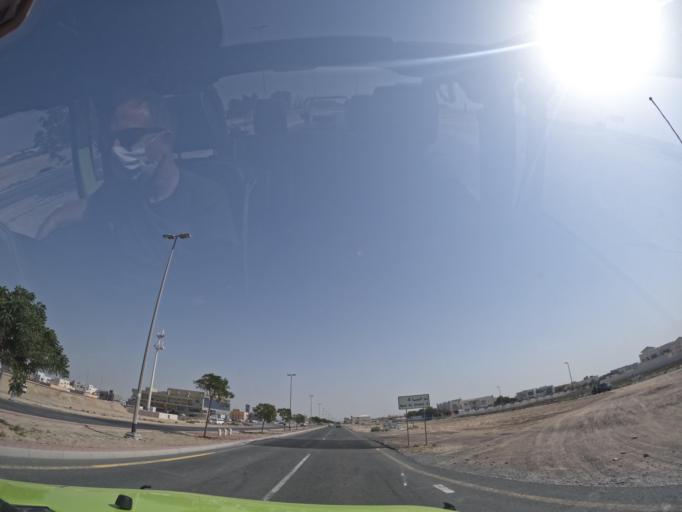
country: AE
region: Dubai
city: Dubai
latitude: 25.1428
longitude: 55.3480
